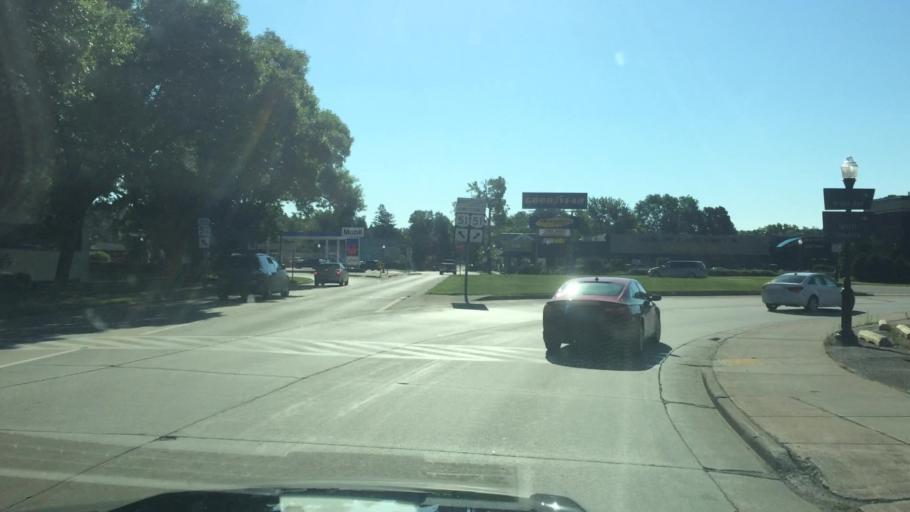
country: US
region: Wisconsin
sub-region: Marathon County
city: Wausau
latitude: 44.9571
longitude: -89.6252
